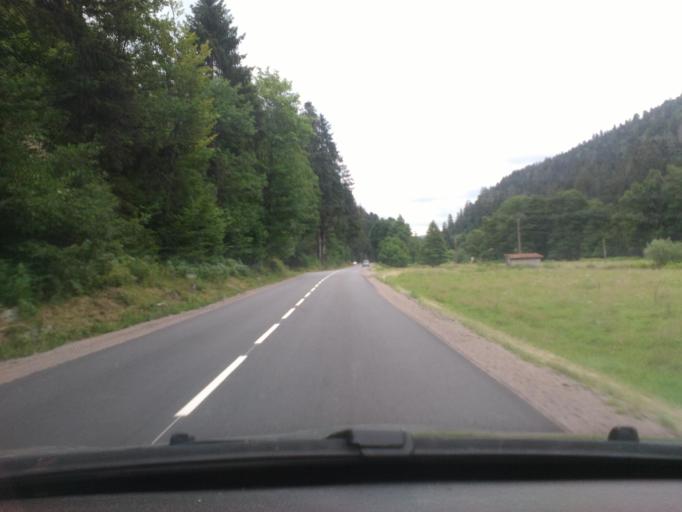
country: FR
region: Lorraine
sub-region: Departement des Vosges
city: Gerardmer
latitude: 48.1157
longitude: 6.8484
